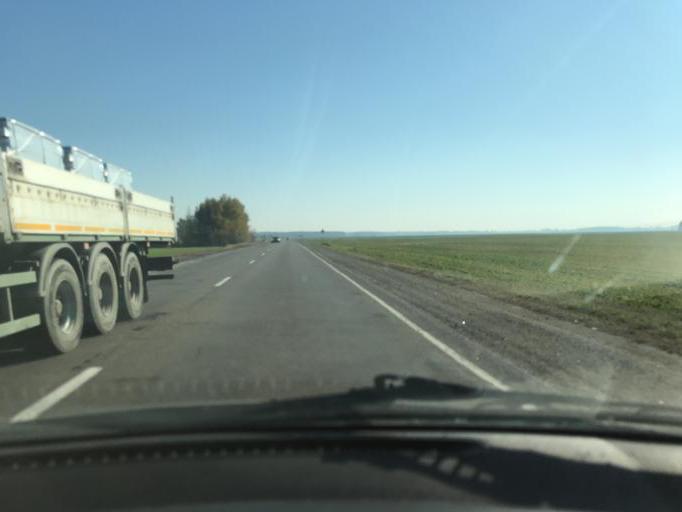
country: BY
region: Brest
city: Luninyets
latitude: 52.2549
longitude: 27.0504
